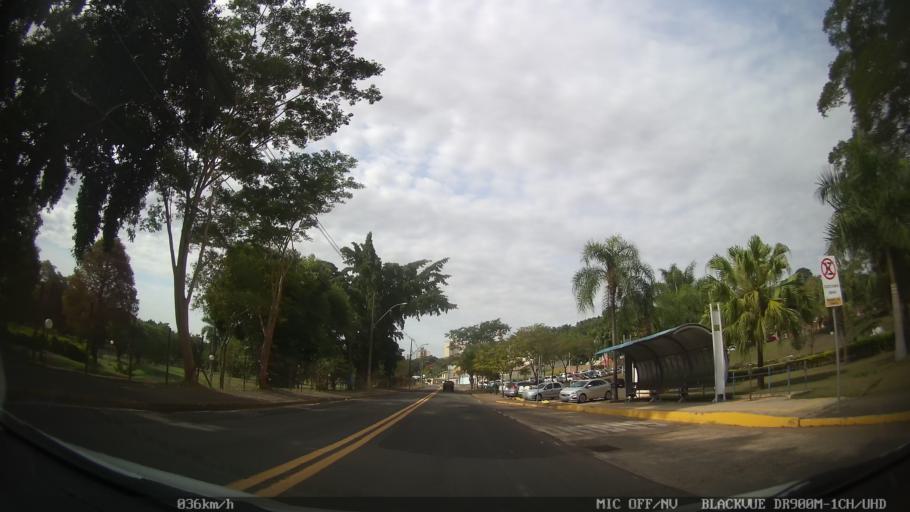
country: BR
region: Sao Paulo
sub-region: Piracicaba
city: Piracicaba
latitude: -22.7282
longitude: -47.6639
